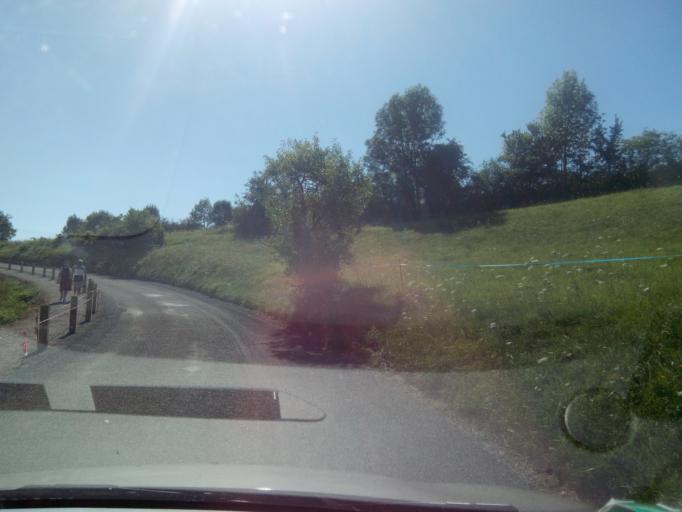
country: FR
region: Midi-Pyrenees
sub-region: Departement du Lot
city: Vayrac
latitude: 45.0036
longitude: 1.7403
